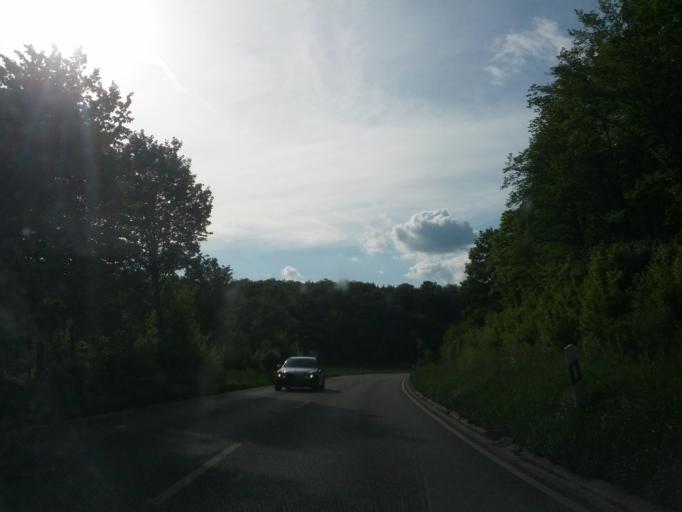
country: DE
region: Baden-Wuerttemberg
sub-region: Regierungsbezirk Stuttgart
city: Aidlingen
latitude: 48.7009
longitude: 8.9192
